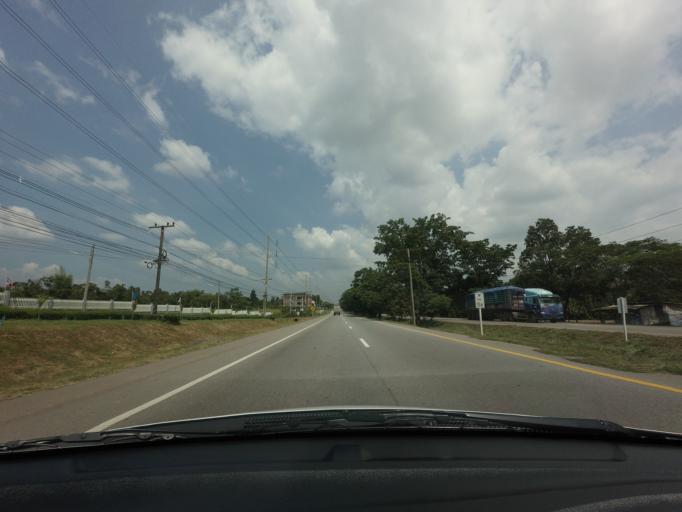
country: TH
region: Prachin Buri
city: Kabin Buri
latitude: 13.9341
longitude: 101.6953
